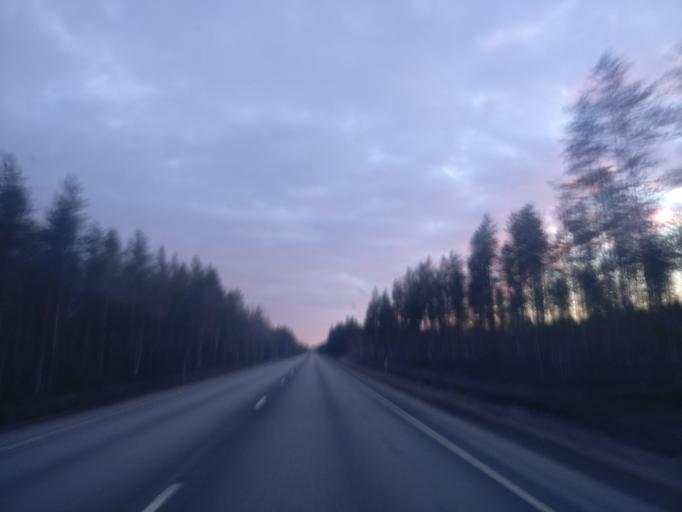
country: FI
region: Northern Ostrobothnia
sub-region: Nivala-Haapajaervi
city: Kaersaemaeki
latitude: 64.0958
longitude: 25.8011
